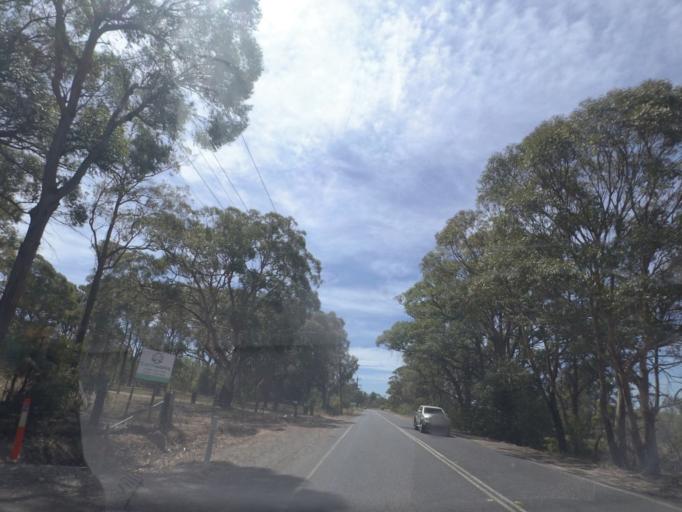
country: AU
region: New South Wales
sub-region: Wollondilly
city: Buxton
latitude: -34.2739
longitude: 150.5758
